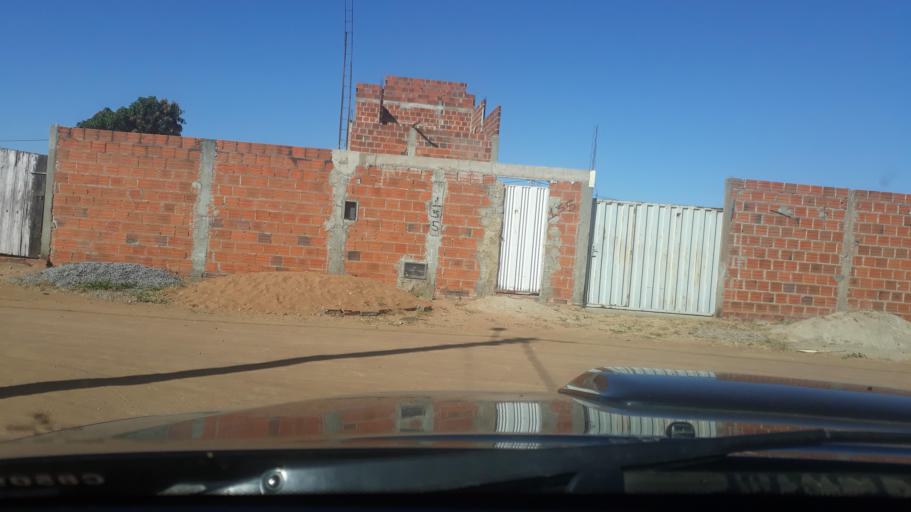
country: BR
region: Bahia
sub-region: Guanambi
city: Guanambi
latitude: -14.1981
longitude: -42.7981
